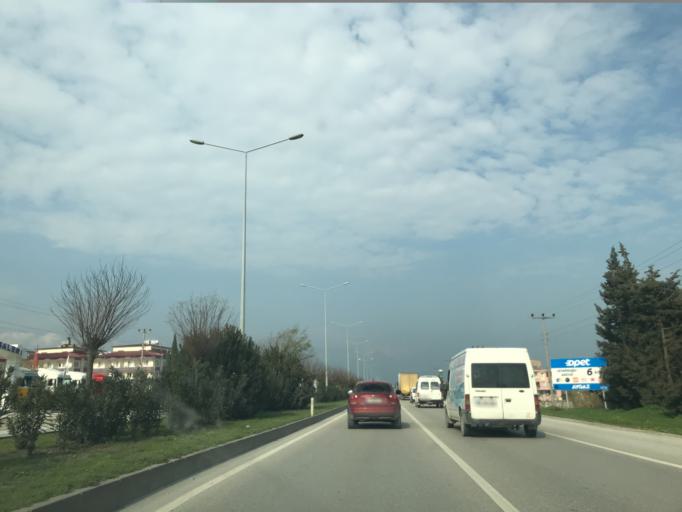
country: TR
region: Hatay
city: Buyuk Dalyan
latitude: 36.2874
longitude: 36.1945
